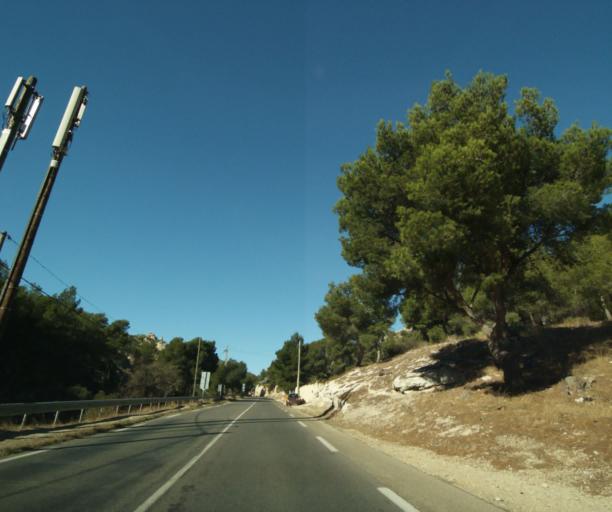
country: FR
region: Provence-Alpes-Cote d'Azur
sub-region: Departement des Bouches-du-Rhone
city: Le Rove
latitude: 43.3579
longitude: 5.2766
